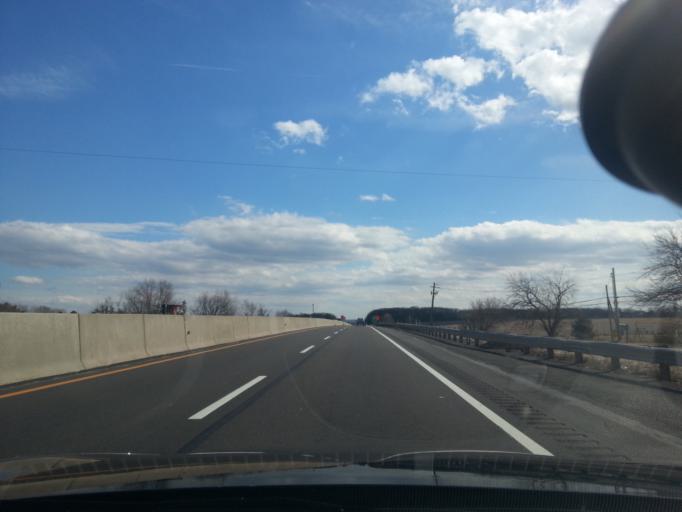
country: US
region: Pennsylvania
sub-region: Montgomery County
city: Harleysville
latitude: 40.2899
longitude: -75.3655
